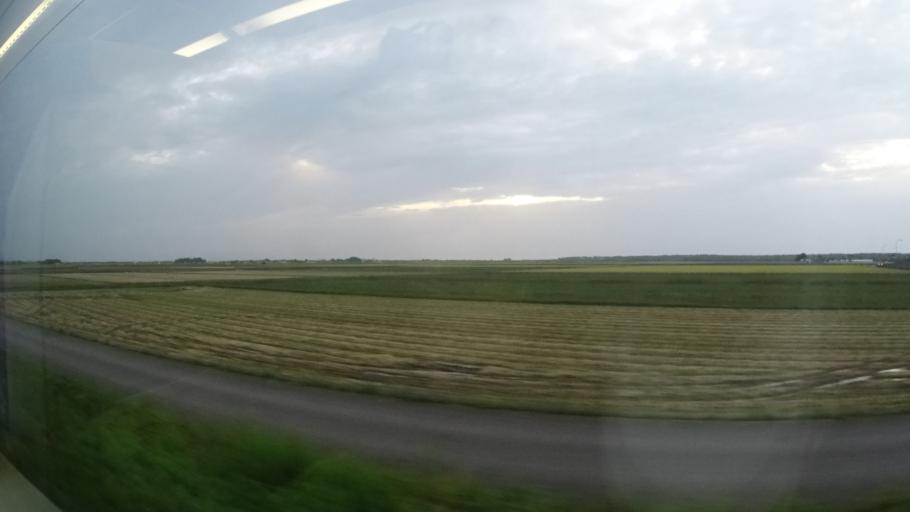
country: JP
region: Niigata
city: Murakami
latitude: 38.1623
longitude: 139.4592
